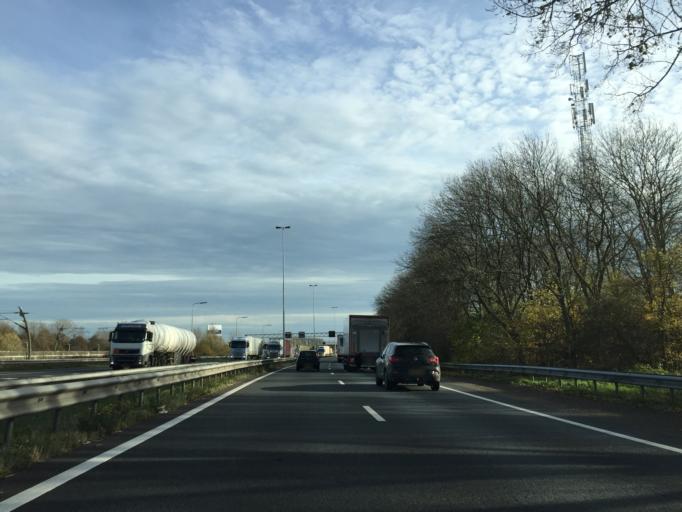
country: NL
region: South Holland
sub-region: Gemeente Gorinchem
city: Gorinchem
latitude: 51.8454
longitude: 4.9950
